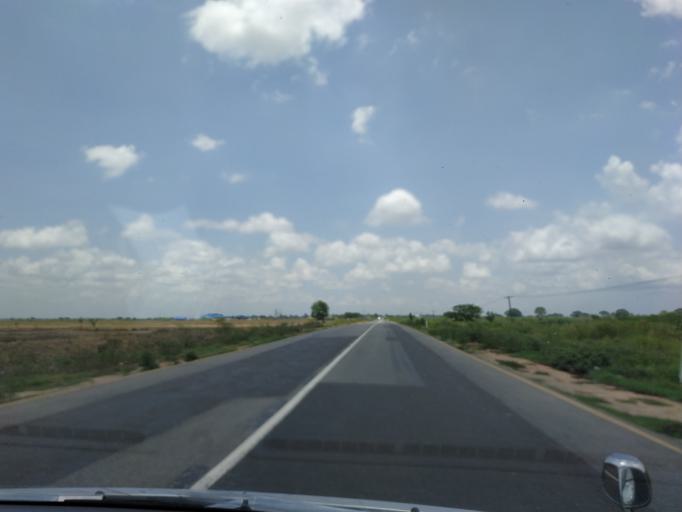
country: MM
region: Bago
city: Thanatpin
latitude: 17.4596
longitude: 96.5999
